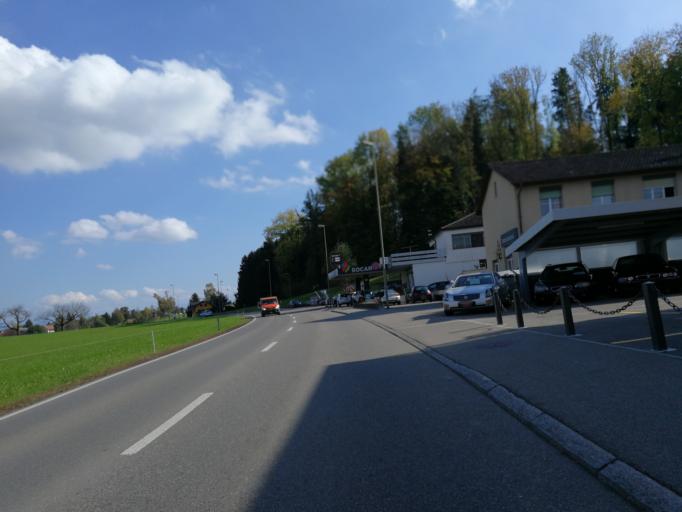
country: CH
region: Zurich
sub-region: Bezirk Meilen
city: Oetwil am See
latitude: 47.2662
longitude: 8.7291
